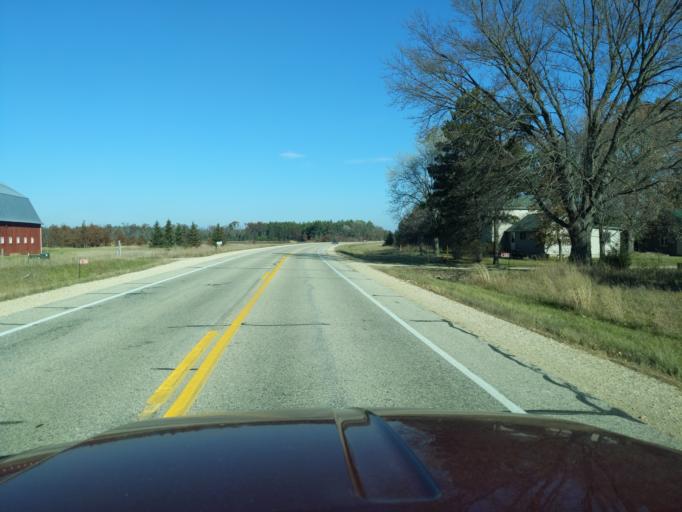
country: US
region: Wisconsin
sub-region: Waushara County
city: Wautoma
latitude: 44.0421
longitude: -89.2972
